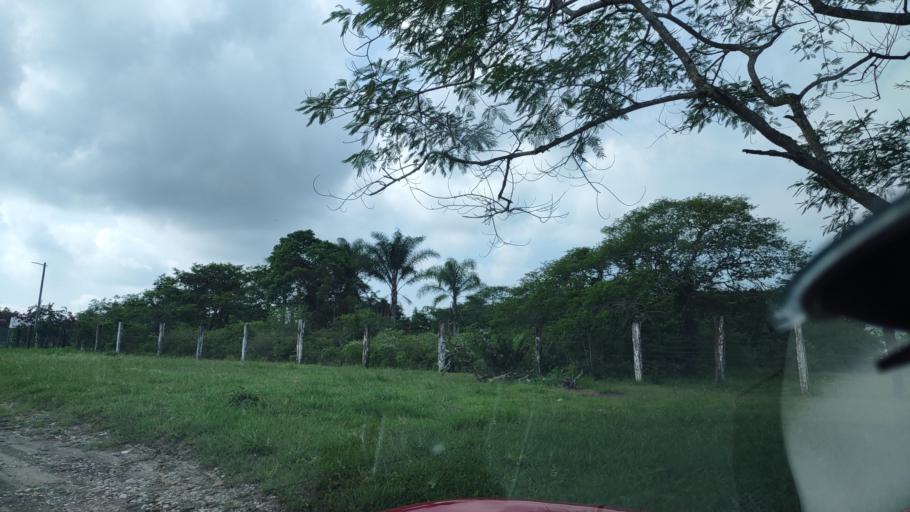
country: MX
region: Veracruz
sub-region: Emiliano Zapata
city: Dos Rios
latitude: 19.4517
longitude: -96.8115
